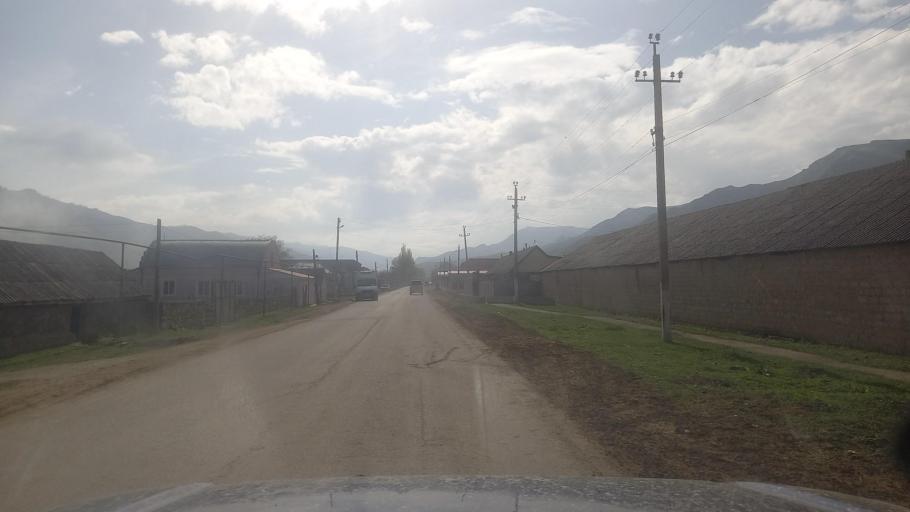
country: RU
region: Kabardino-Balkariya
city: Kamennomostskoye
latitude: 43.7317
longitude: 42.9528
